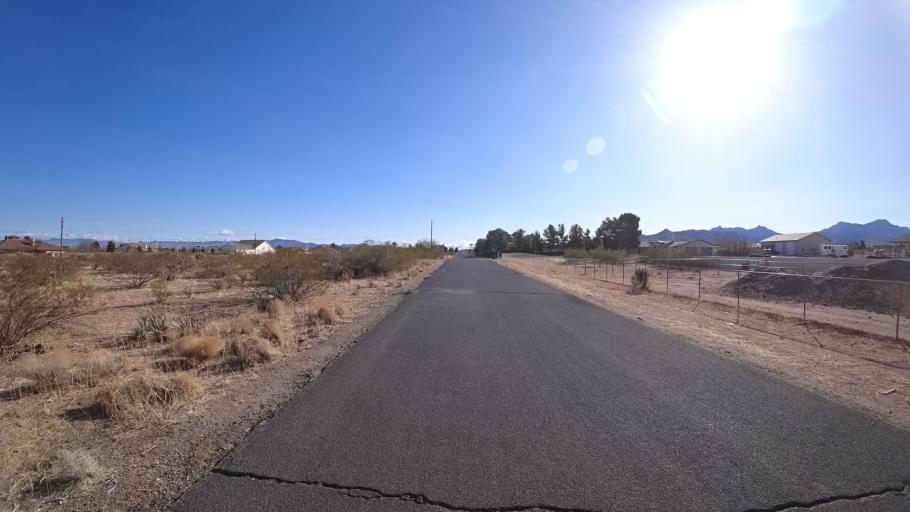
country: US
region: Arizona
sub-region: Mohave County
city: Kingman
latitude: 35.2065
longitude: -114.0013
